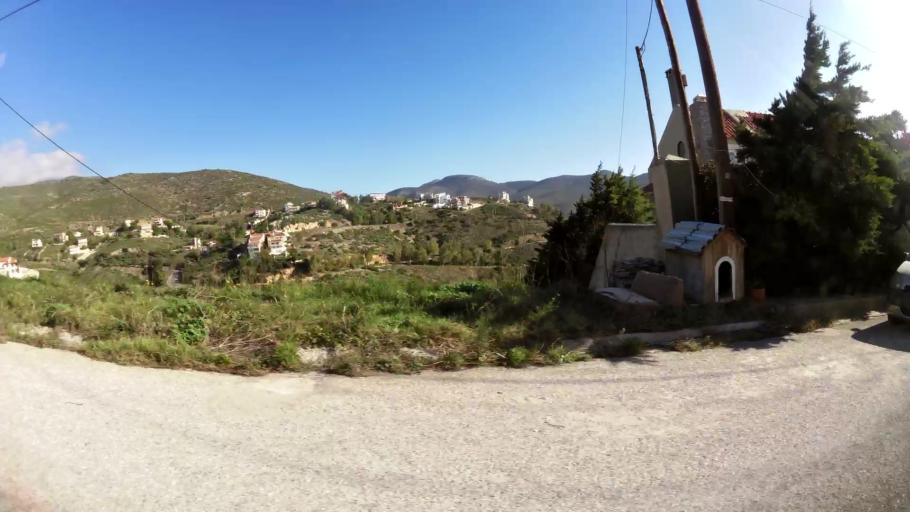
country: GR
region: Attica
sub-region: Nomarchia Anatolikis Attikis
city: Dhrafi
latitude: 38.0394
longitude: 23.8971
